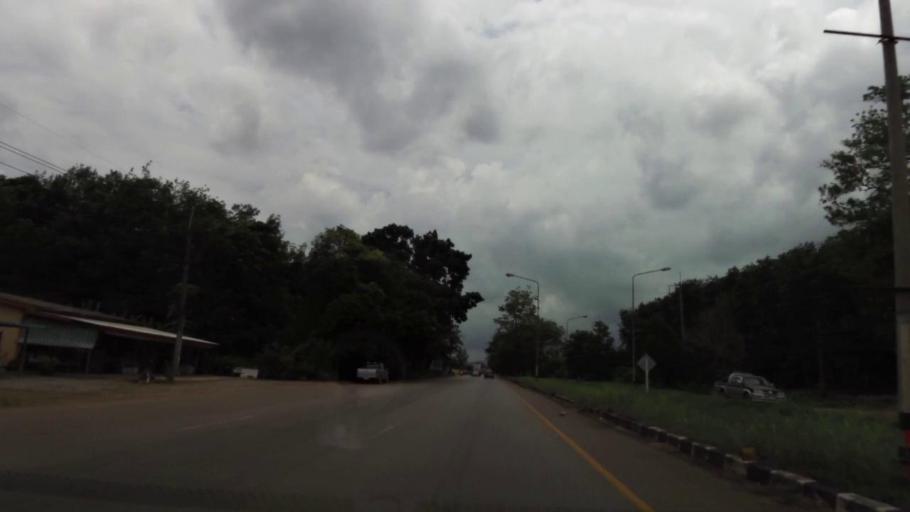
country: TH
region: Rayong
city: Wang Chan
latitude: 12.8781
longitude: 101.5688
